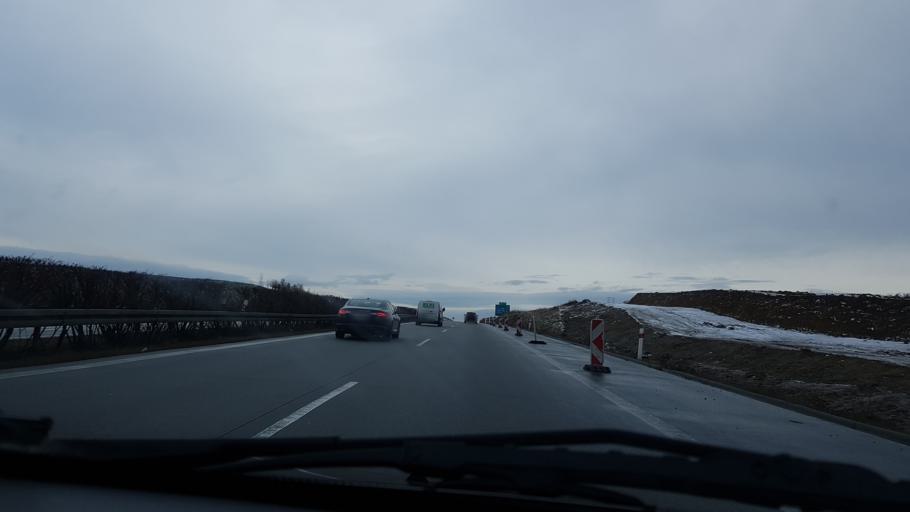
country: CZ
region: Olomoucky
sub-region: Okres Prerov
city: Lipnik nad Becvou
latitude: 49.5475
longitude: 17.5735
